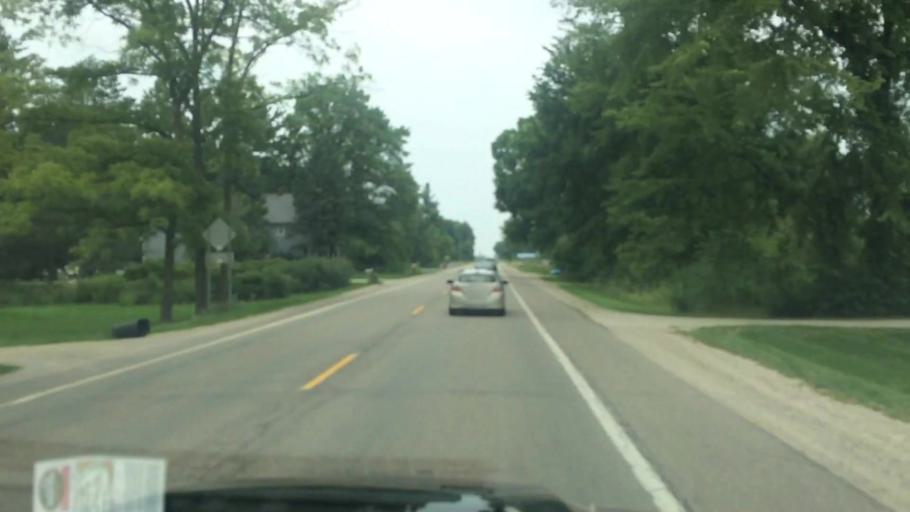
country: US
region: Michigan
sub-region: Huron County
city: Bad Axe
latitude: 43.8966
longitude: -83.0034
